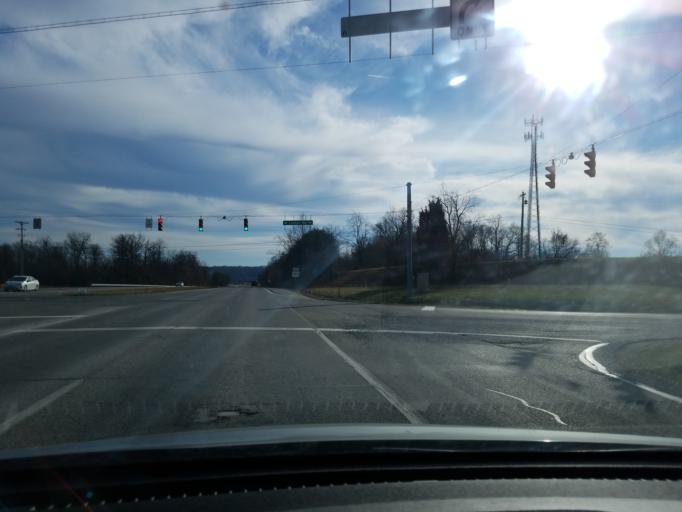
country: US
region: Indiana
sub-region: Floyd County
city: Galena
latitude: 38.3266
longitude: -85.8983
